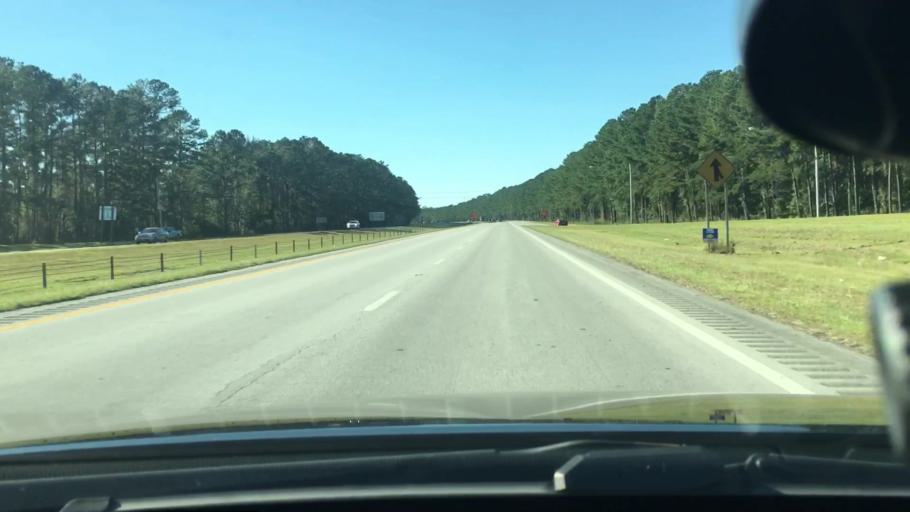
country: US
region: North Carolina
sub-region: Craven County
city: Trent Woods
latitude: 35.1136
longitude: -77.0986
